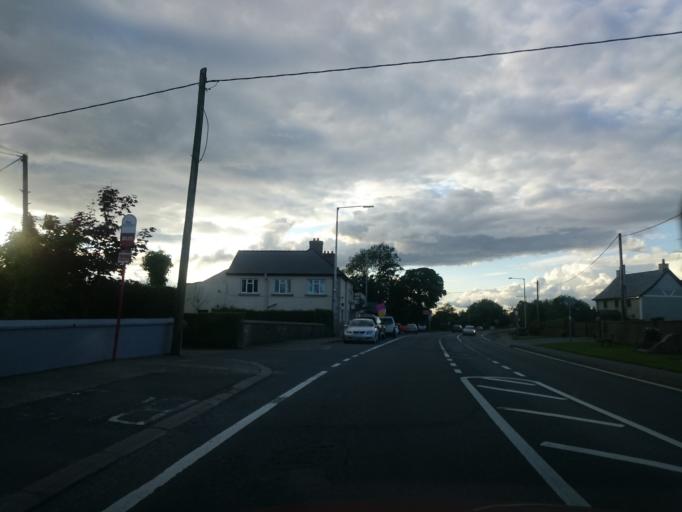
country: IE
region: Leinster
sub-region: Loch Garman
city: Enniscorthy
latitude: 52.4241
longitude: -6.5310
